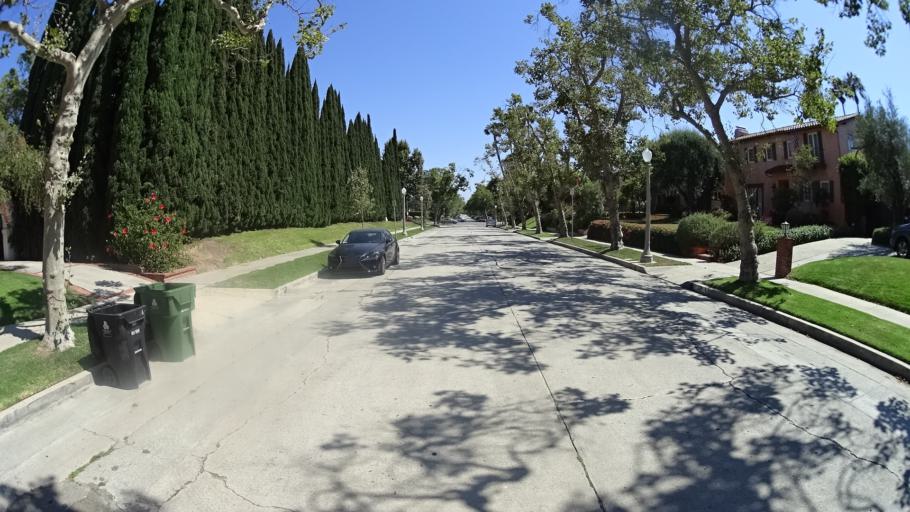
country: US
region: California
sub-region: Los Angeles County
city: Hollywood
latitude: 34.0699
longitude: -118.3372
